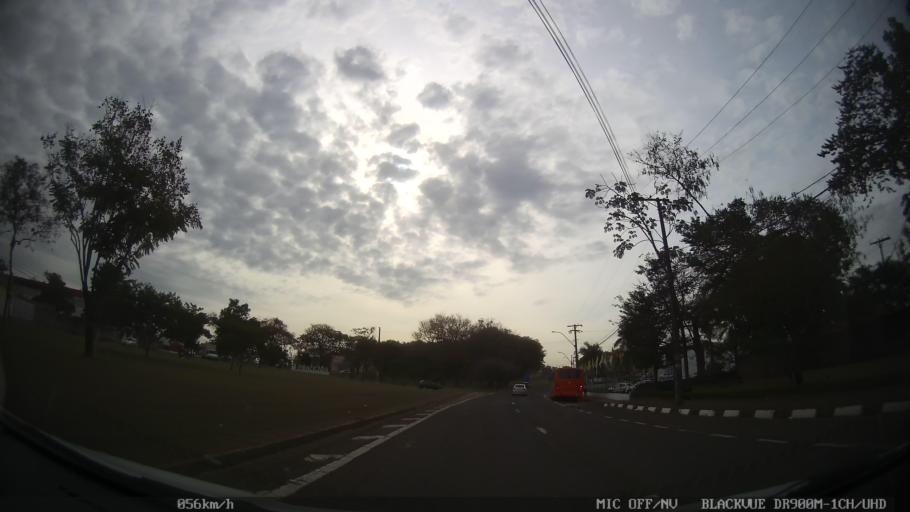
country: BR
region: Sao Paulo
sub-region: Piracicaba
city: Piracicaba
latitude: -22.7321
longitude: -47.6101
